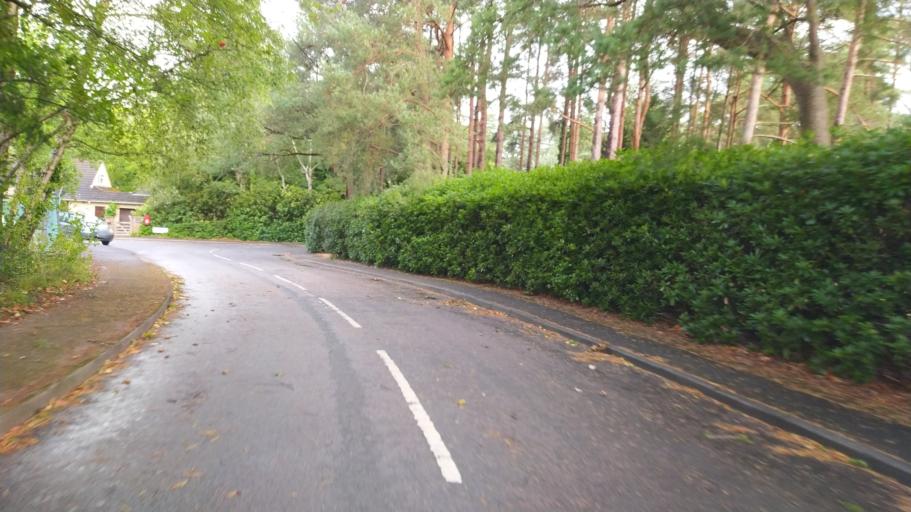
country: GB
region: England
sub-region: Dorset
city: St Leonards
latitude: 50.8366
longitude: -1.8318
